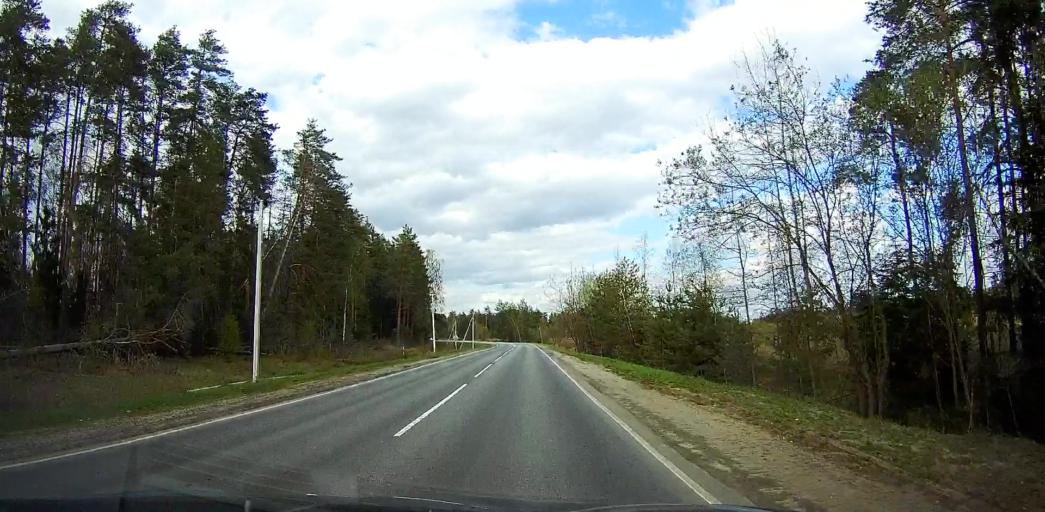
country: RU
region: Moskovskaya
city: Rakhmanovo
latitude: 55.7251
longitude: 38.6281
